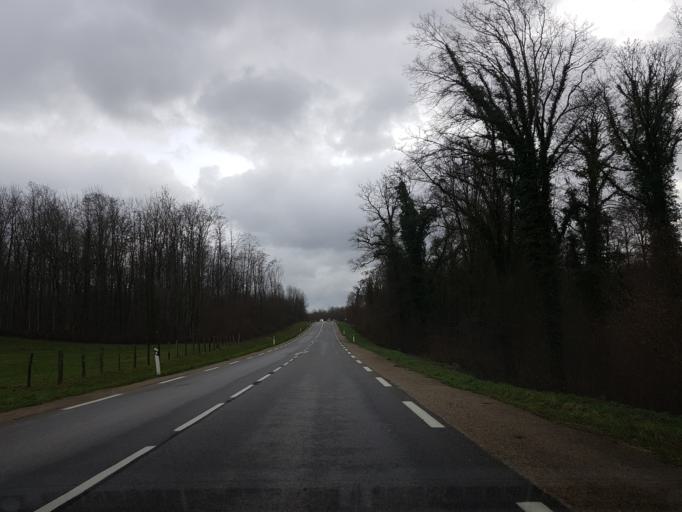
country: FR
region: Champagne-Ardenne
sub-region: Departement de la Haute-Marne
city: Fayl-Billot
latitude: 47.7997
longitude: 5.5618
